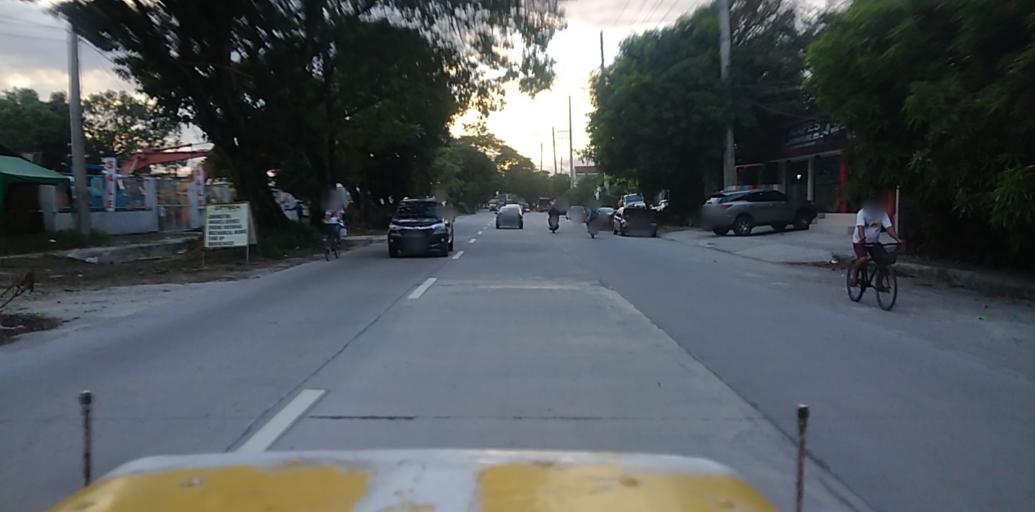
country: PH
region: Central Luzon
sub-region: Province of Pampanga
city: Calibutbut
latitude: 15.1162
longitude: 120.5991
